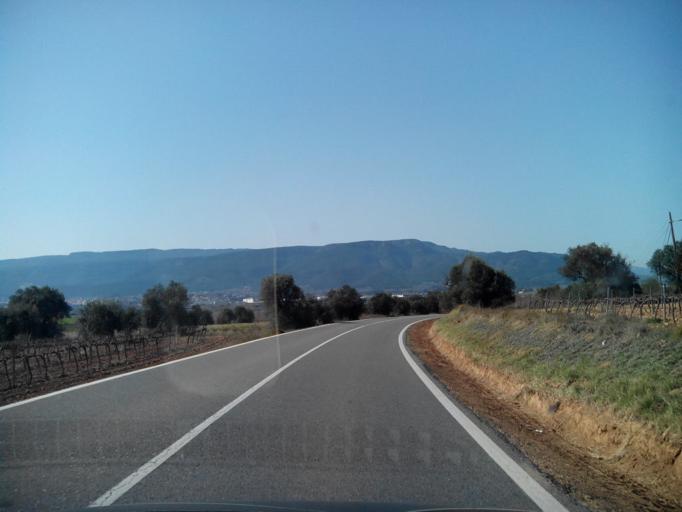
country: ES
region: Catalonia
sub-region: Provincia de Tarragona
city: Montblanc
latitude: 41.3984
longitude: 1.1849
